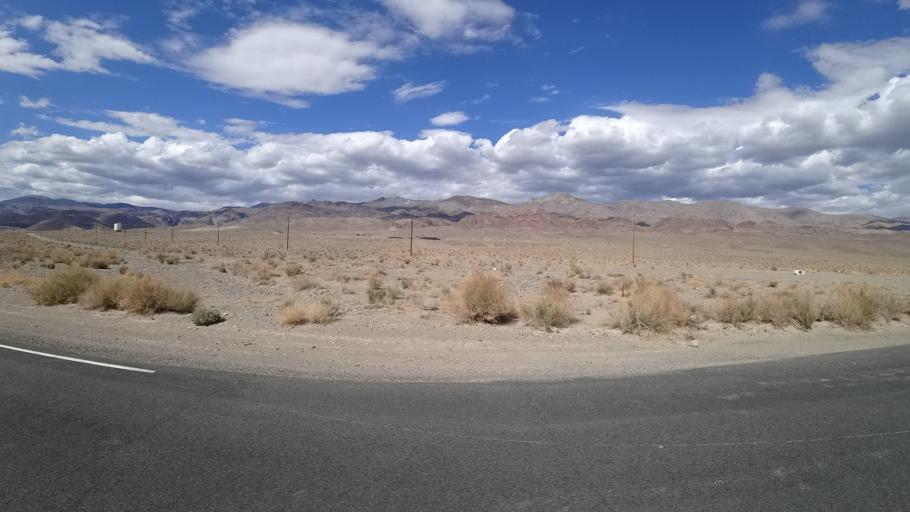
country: US
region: California
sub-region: Inyo County
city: Lone Pine
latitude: 36.4867
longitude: -117.8672
